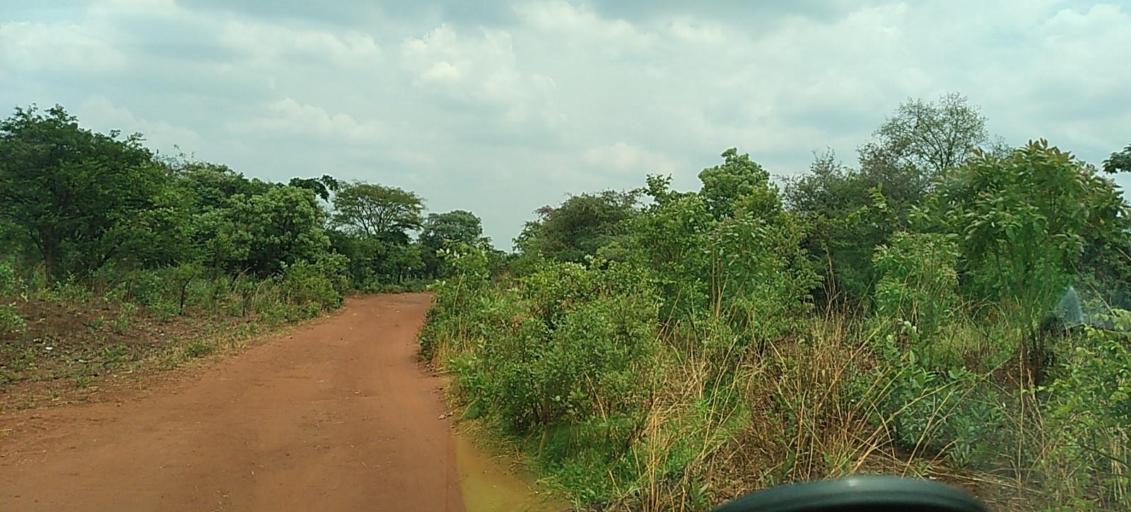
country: ZM
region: North-Western
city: Kansanshi
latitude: -12.0461
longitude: 26.3828
